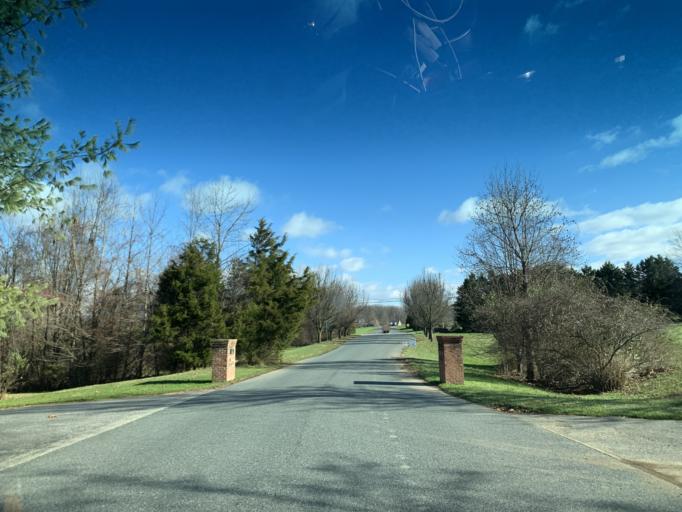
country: US
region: Maryland
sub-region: Harford County
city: South Bel Air
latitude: 39.5683
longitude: -76.2556
